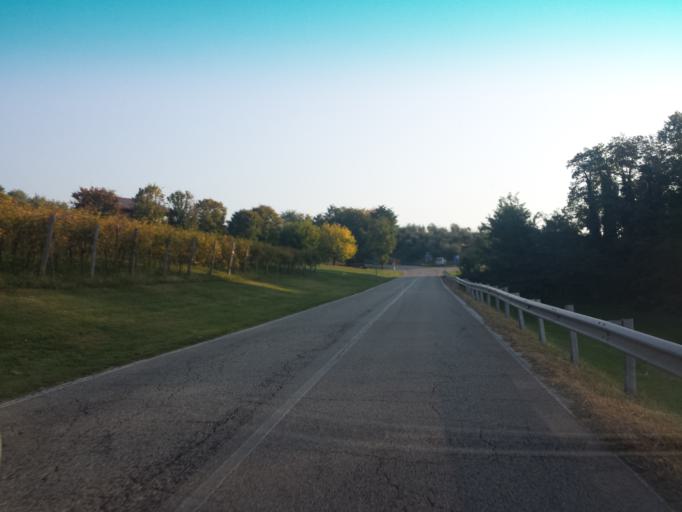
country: IT
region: Veneto
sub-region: Provincia di Vicenza
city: Mason Vicentino
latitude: 45.7246
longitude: 11.5812
